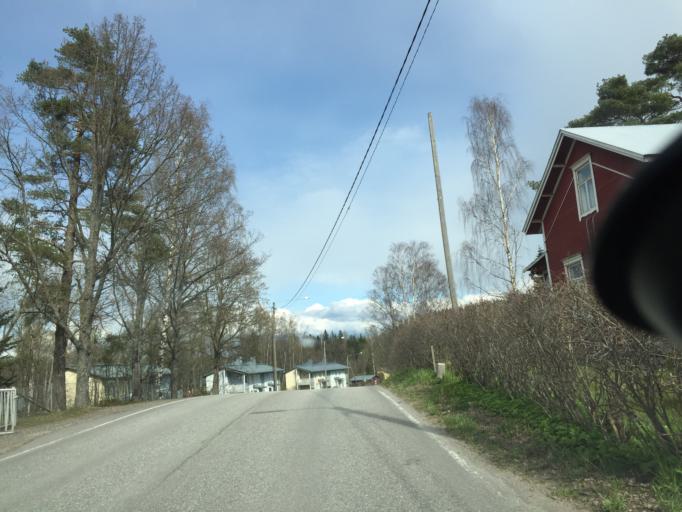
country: FI
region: Varsinais-Suomi
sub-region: Salo
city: Saerkisalo
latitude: 59.9892
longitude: 23.0351
